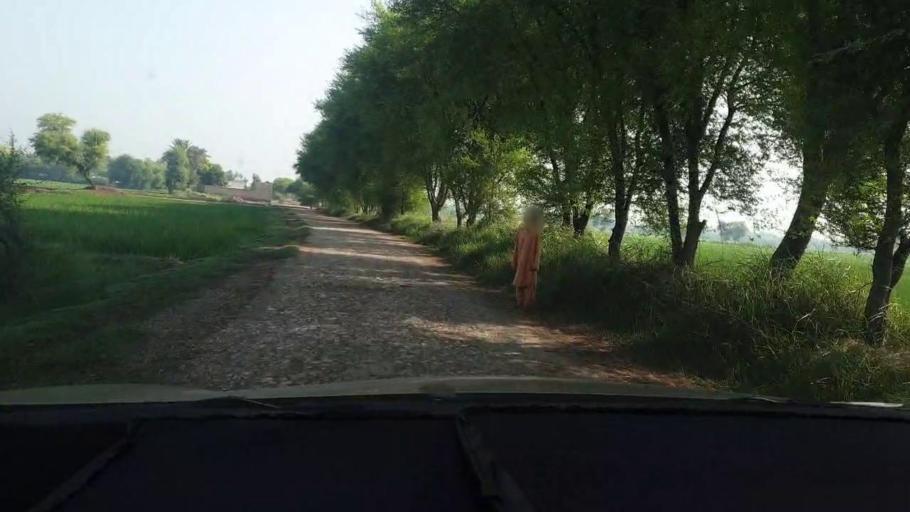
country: PK
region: Sindh
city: Kambar
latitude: 27.6000
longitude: 68.1113
